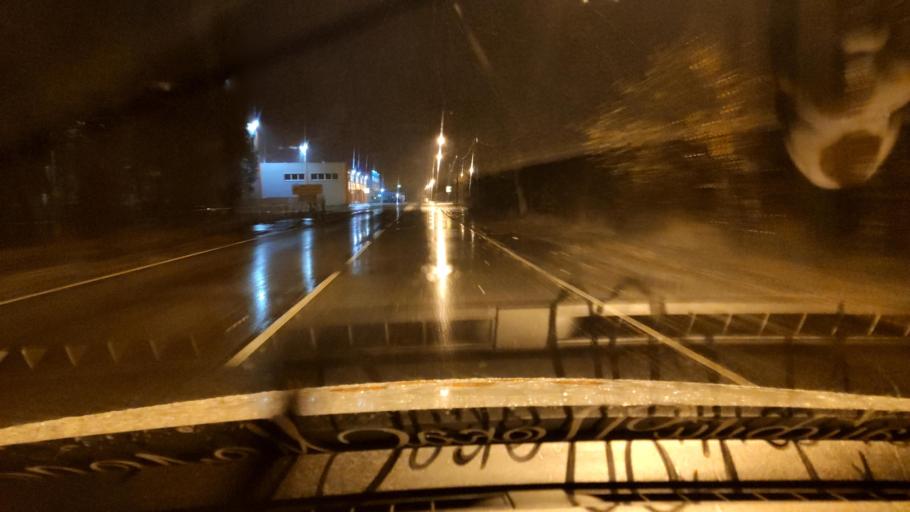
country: RU
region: Voronezj
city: Somovo
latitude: 51.7182
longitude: 39.2943
